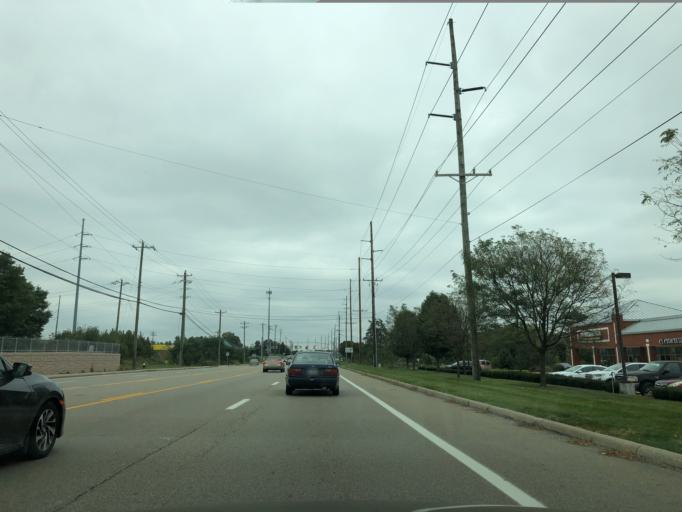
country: US
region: Ohio
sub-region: Hamilton County
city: Sixteen Mile Stand
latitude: 39.2864
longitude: -84.3080
